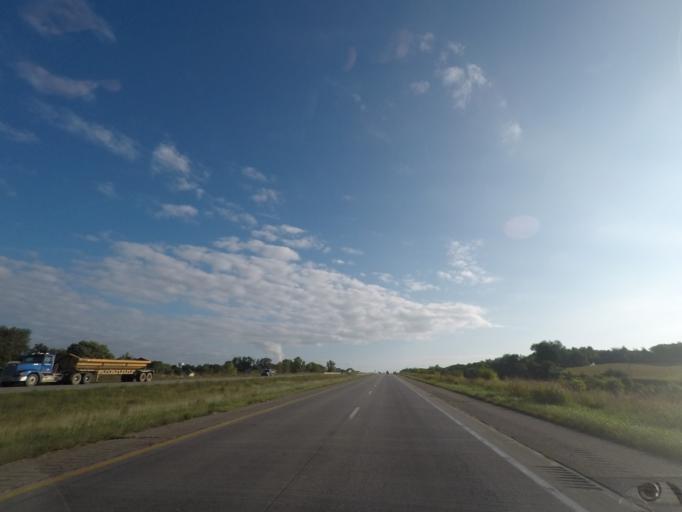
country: US
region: Iowa
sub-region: Polk County
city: Pleasant Hill
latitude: 41.5805
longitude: -93.5103
